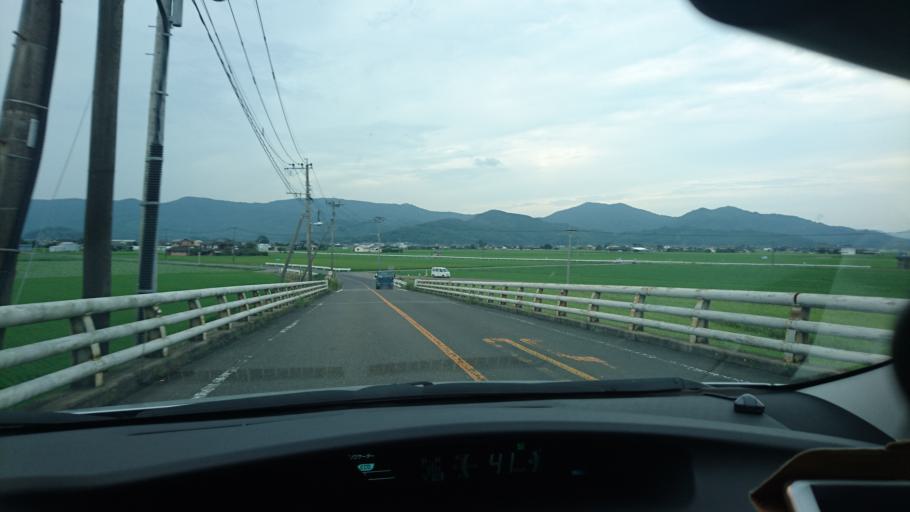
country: JP
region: Saga Prefecture
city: Takeocho-takeo
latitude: 33.1996
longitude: 130.1164
